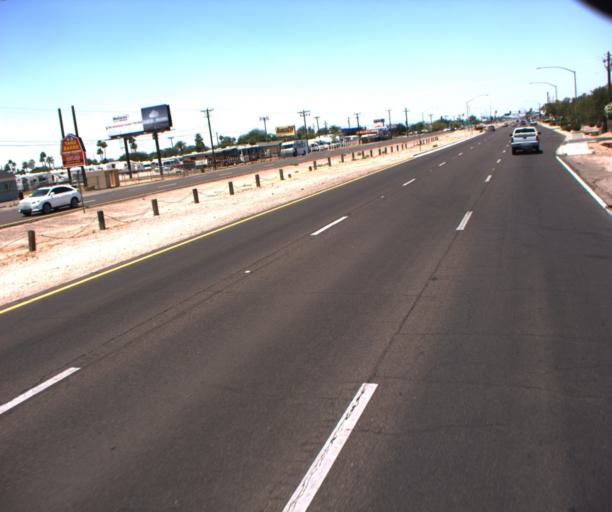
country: US
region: Arizona
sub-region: Pinal County
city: Apache Junction
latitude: 33.4154
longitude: -111.6296
